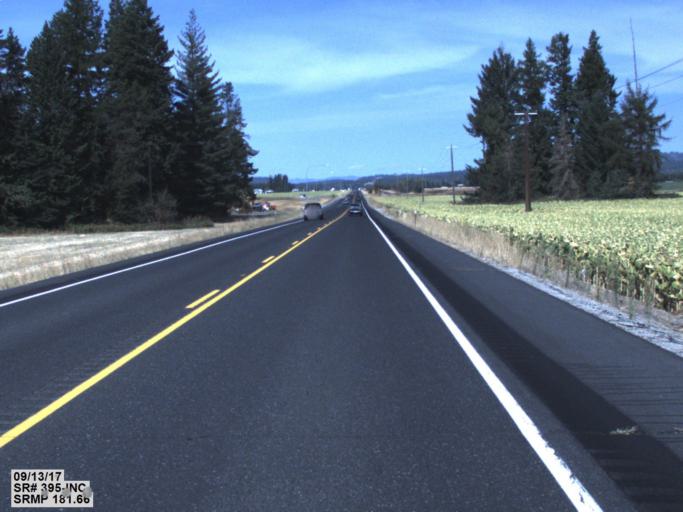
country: US
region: Washington
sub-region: Spokane County
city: Deer Park
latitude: 47.9666
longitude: -117.5059
